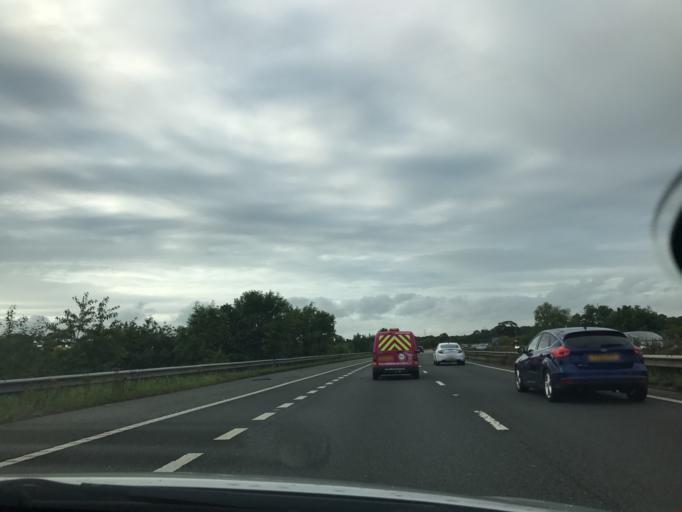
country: GB
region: England
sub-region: Cheshire West and Chester
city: Hoole
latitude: 53.2160
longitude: -2.8583
